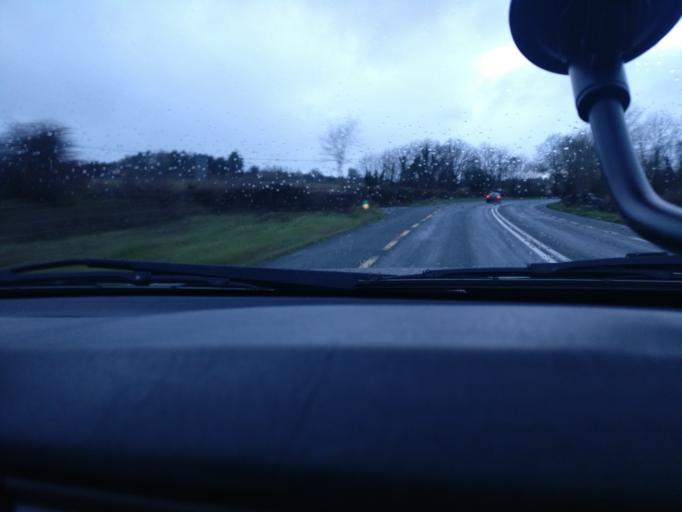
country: IE
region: Connaught
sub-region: County Galway
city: Ballinasloe
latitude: 53.3121
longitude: -8.2642
